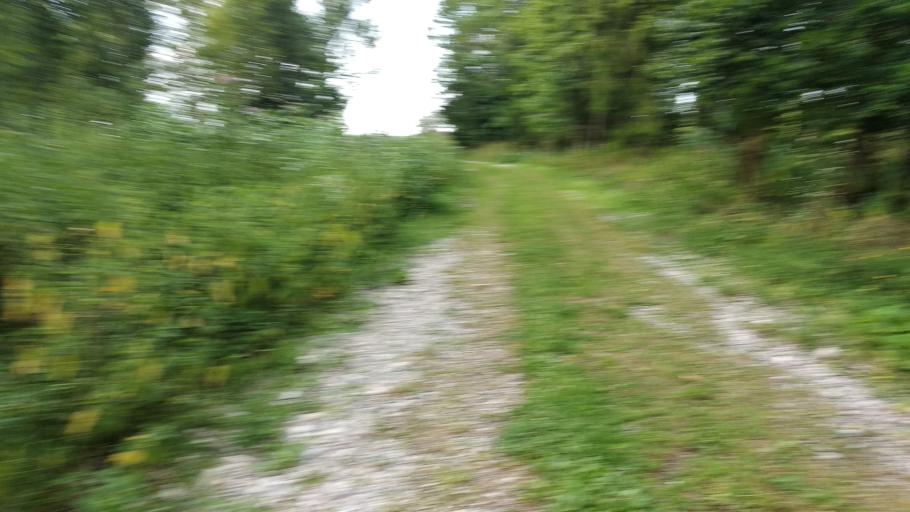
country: DE
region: Bavaria
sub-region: Swabia
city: Kronburg
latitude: 47.9018
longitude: 10.1471
